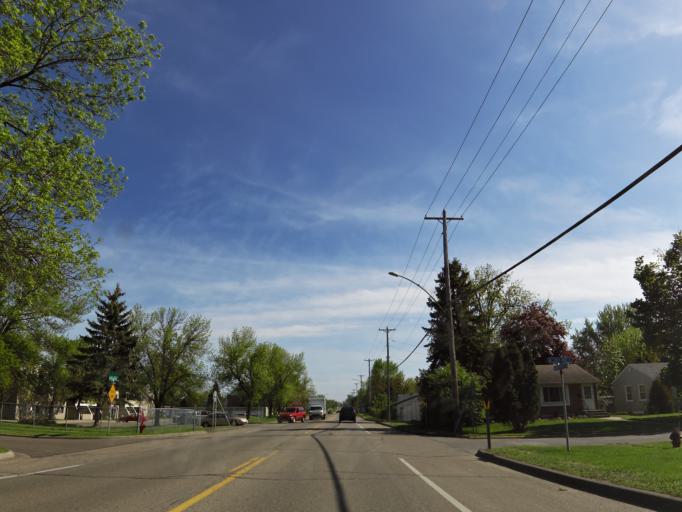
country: US
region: Minnesota
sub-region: Ramsey County
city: North Saint Paul
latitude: 45.0097
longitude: -92.9848
